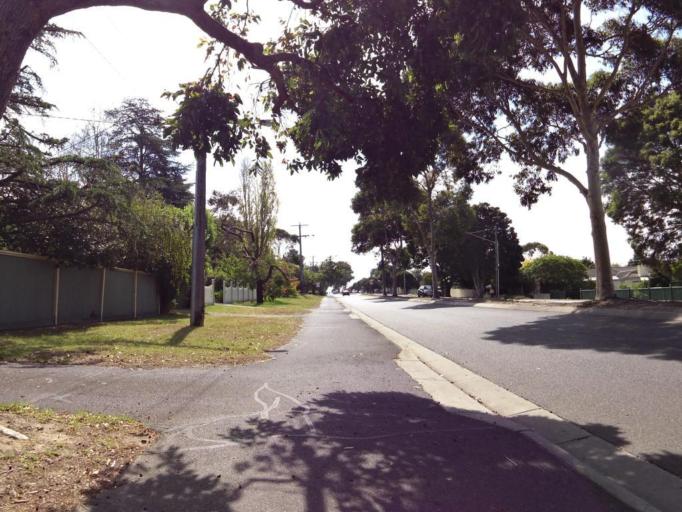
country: AU
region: Victoria
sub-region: Mornington Peninsula
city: Somerville
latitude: -38.2286
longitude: 145.1800
